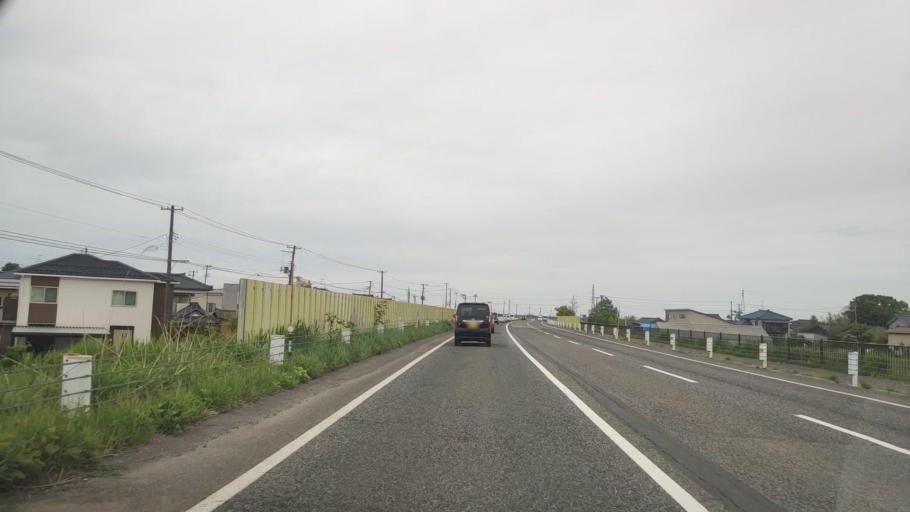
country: JP
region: Niigata
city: Niitsu-honcho
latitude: 37.7973
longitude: 139.1065
